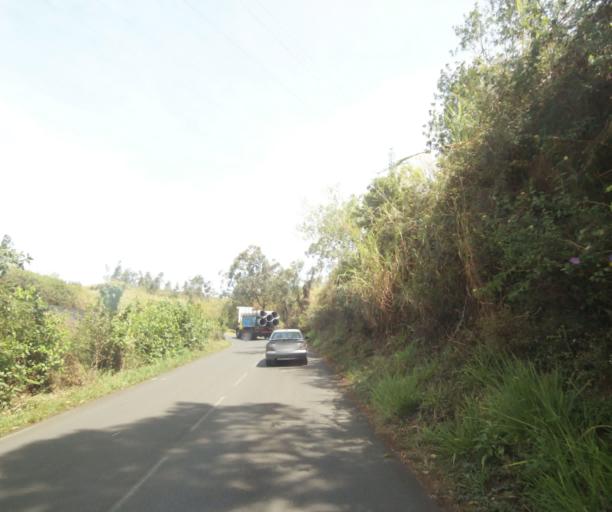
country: RE
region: Reunion
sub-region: Reunion
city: Saint-Paul
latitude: -21.0403
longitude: 55.3176
